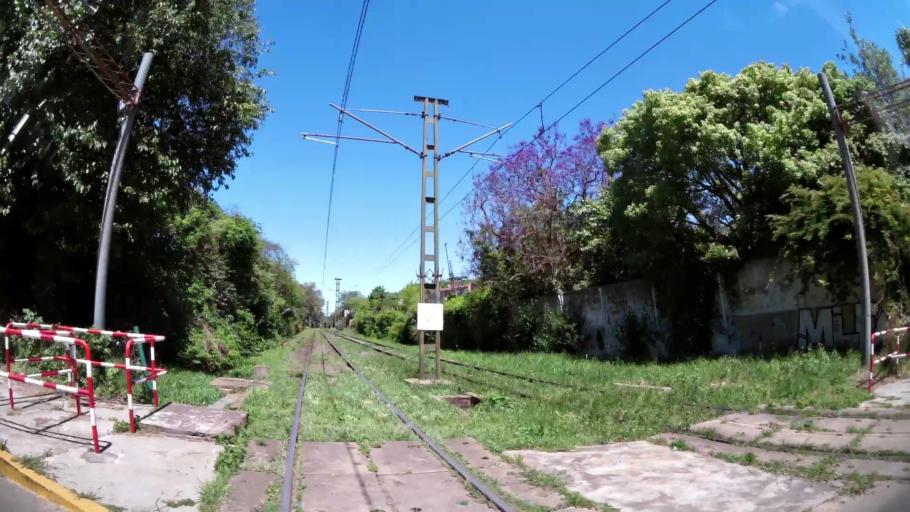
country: AR
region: Buenos Aires
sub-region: Partido de San Isidro
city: San Isidro
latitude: -34.4566
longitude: -58.5176
